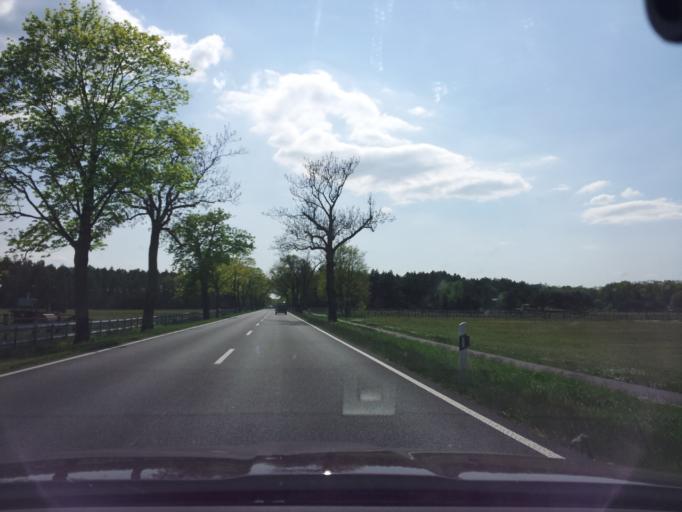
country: DE
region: Brandenburg
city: Treuenbrietzen
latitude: 52.1215
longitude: 12.8969
